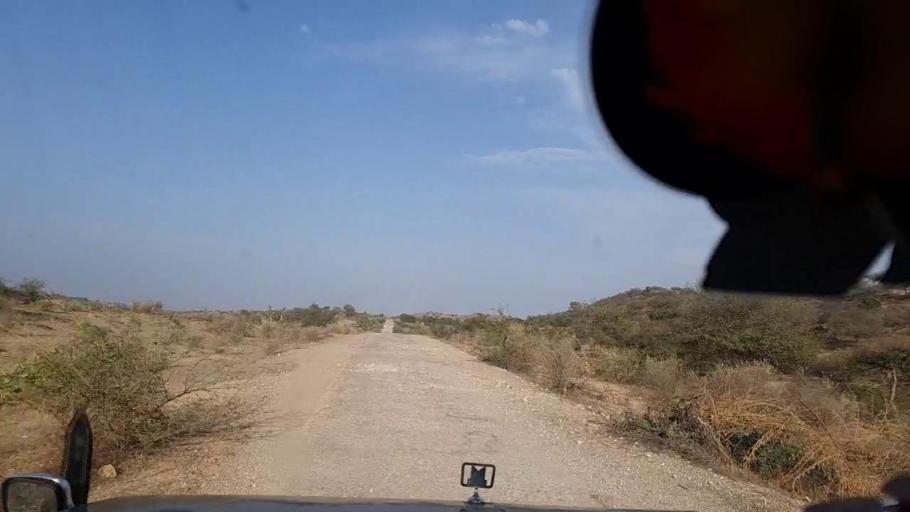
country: PK
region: Sindh
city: Diplo
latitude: 24.5576
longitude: 69.4733
